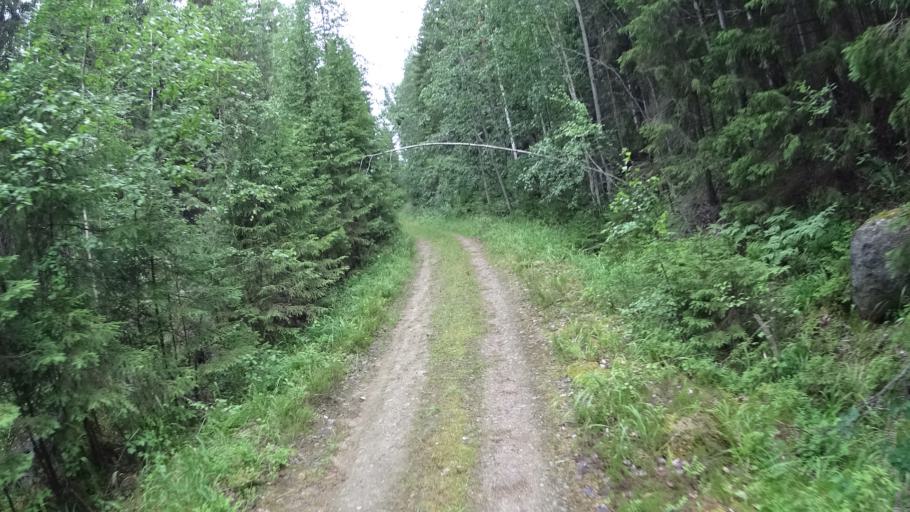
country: FI
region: Southern Savonia
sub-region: Mikkeli
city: Maentyharju
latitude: 61.1856
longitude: 26.8289
